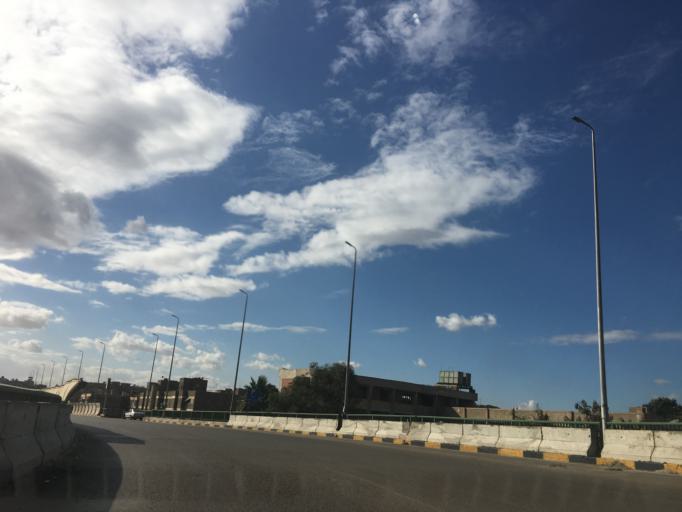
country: EG
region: Al Jizah
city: Al Jizah
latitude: 30.0289
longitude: 31.1991
